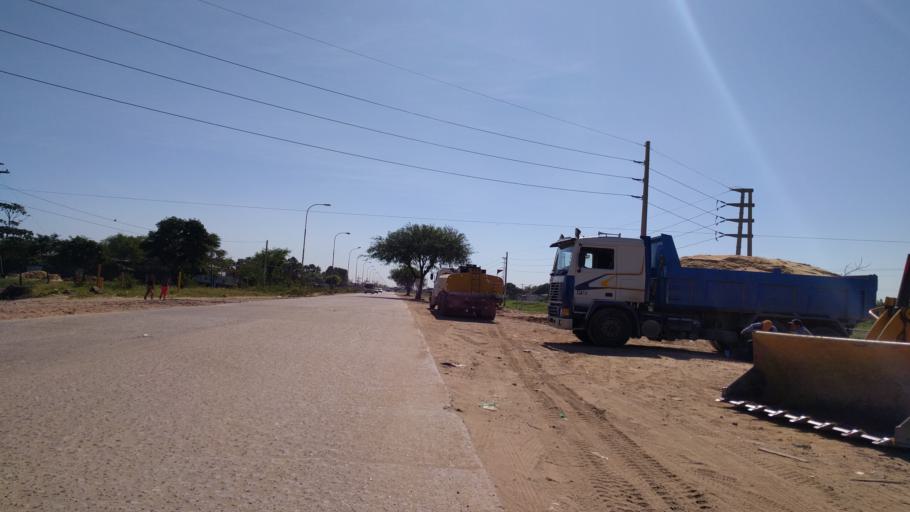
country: BO
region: Santa Cruz
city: Santa Cruz de la Sierra
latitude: -17.8733
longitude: -63.1927
